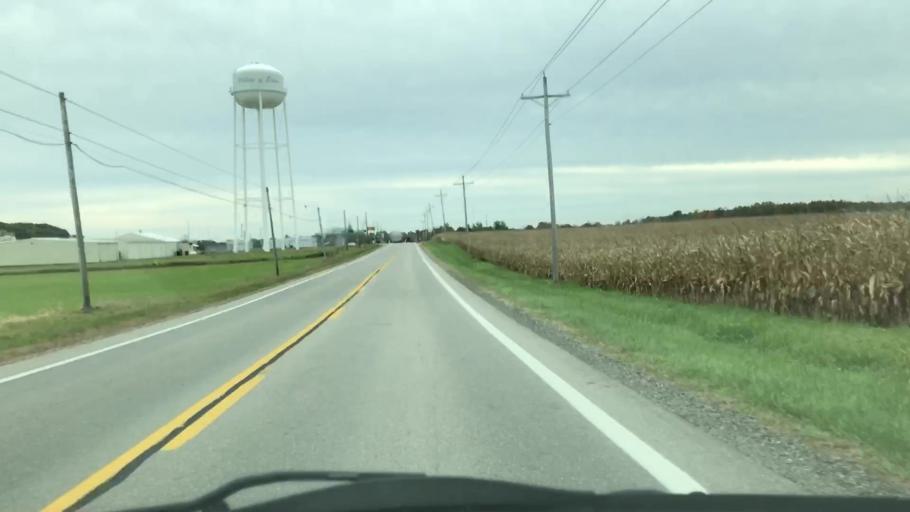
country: US
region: Ohio
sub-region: Williams County
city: Edgerton
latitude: 41.5738
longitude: -84.7692
